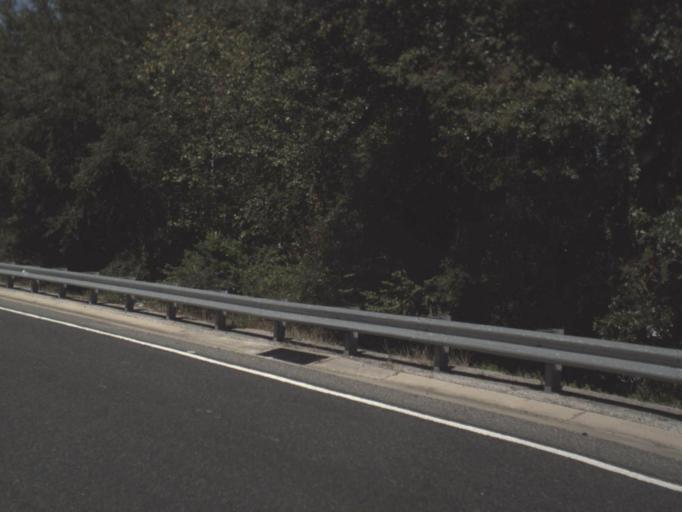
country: US
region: Florida
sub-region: Sumter County
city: Wildwood
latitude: 28.8389
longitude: -82.0486
